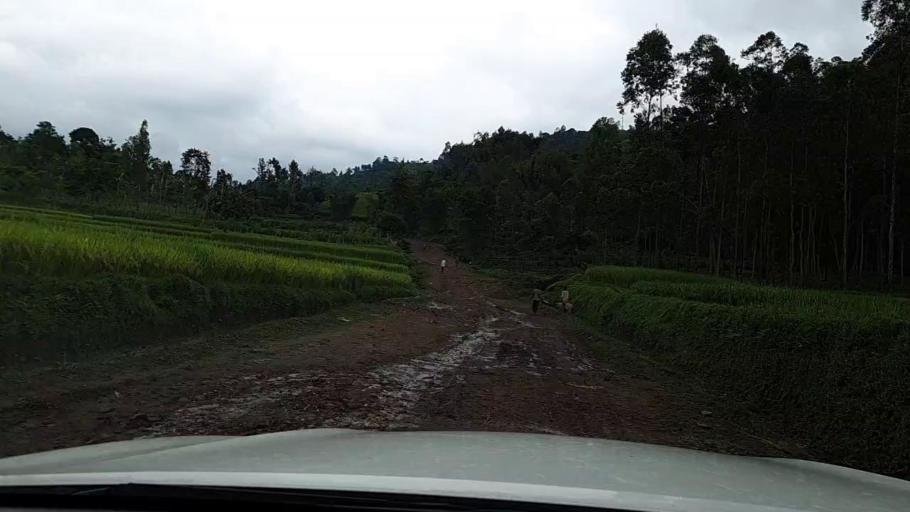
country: RW
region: Western Province
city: Cyangugu
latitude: -2.5638
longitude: 29.0357
